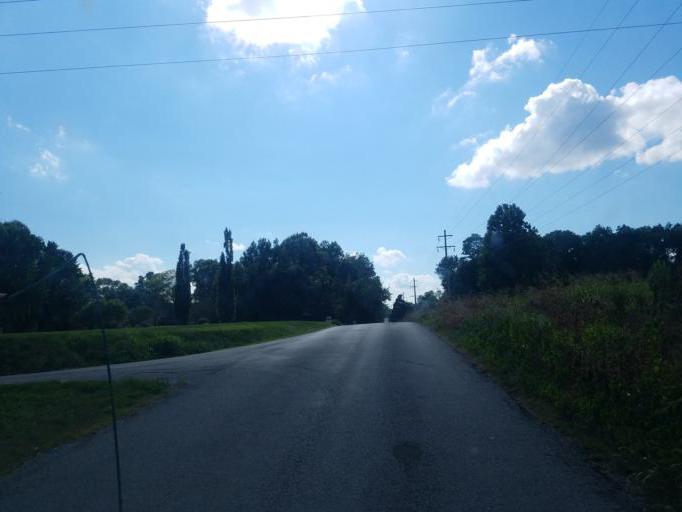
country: US
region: Illinois
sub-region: Jackson County
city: Murphysboro
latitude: 37.7090
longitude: -89.3051
